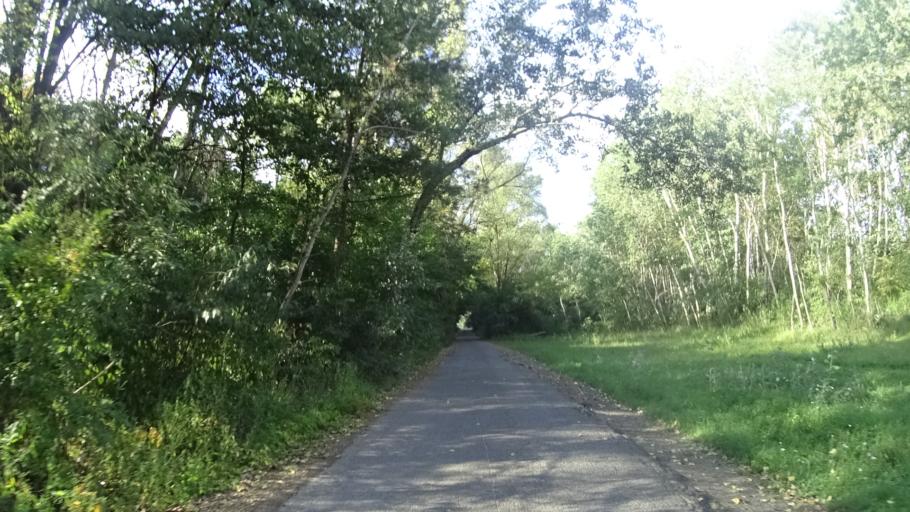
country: AT
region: Lower Austria
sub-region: Politischer Bezirk Mistelbach
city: Rabensburg
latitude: 48.5978
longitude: 16.9499
